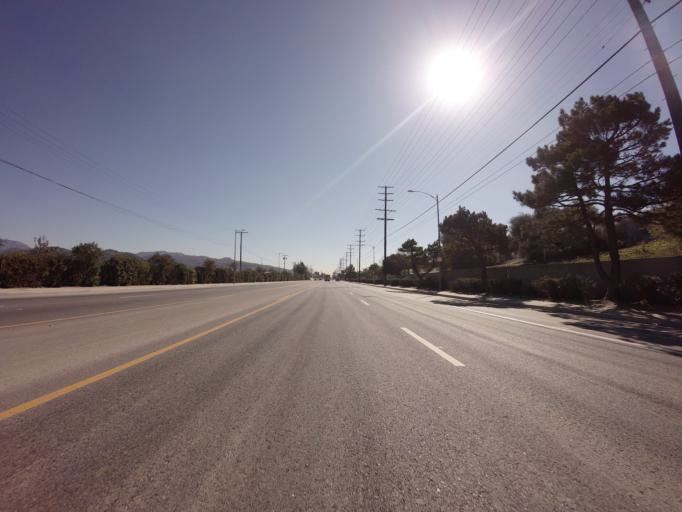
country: US
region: California
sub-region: Los Angeles County
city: North Hollywood
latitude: 34.2419
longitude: -118.3793
